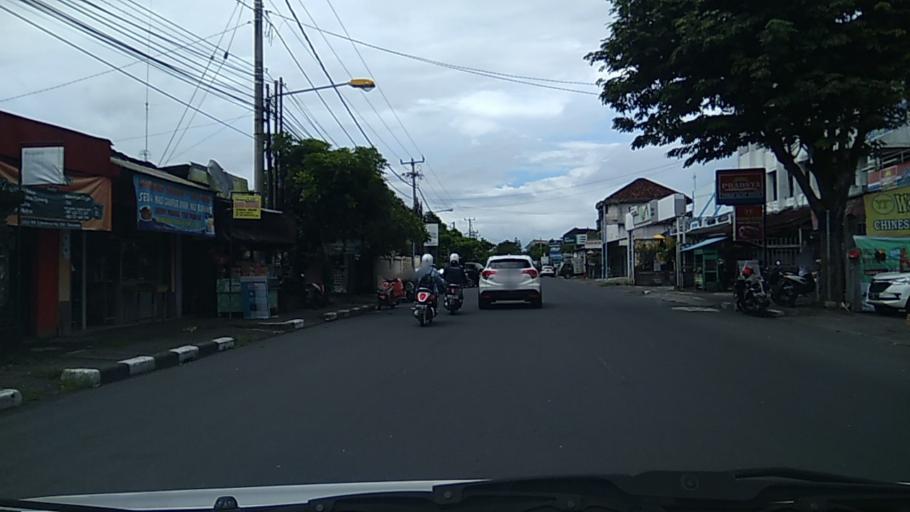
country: ID
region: Bali
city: Banjar Kertajiwa
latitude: -8.6420
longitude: 115.2510
